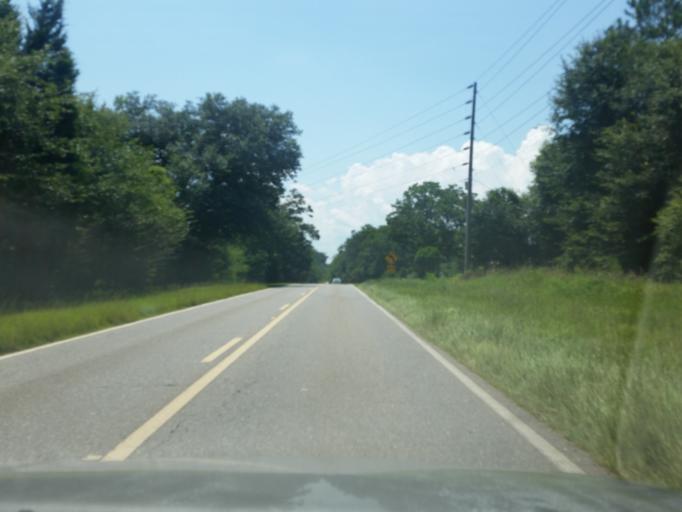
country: US
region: Alabama
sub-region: Baldwin County
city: Robertsdale
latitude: 30.6260
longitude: -87.6607
